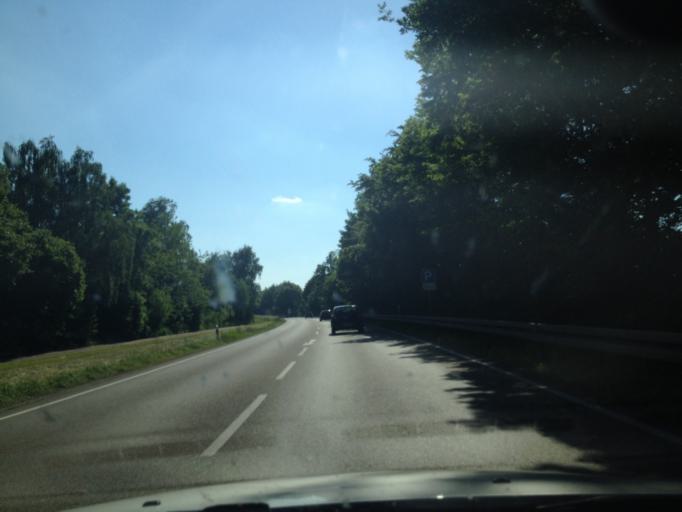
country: DE
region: Bavaria
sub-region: Swabia
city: Kuhbach
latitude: 48.4844
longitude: 11.1693
